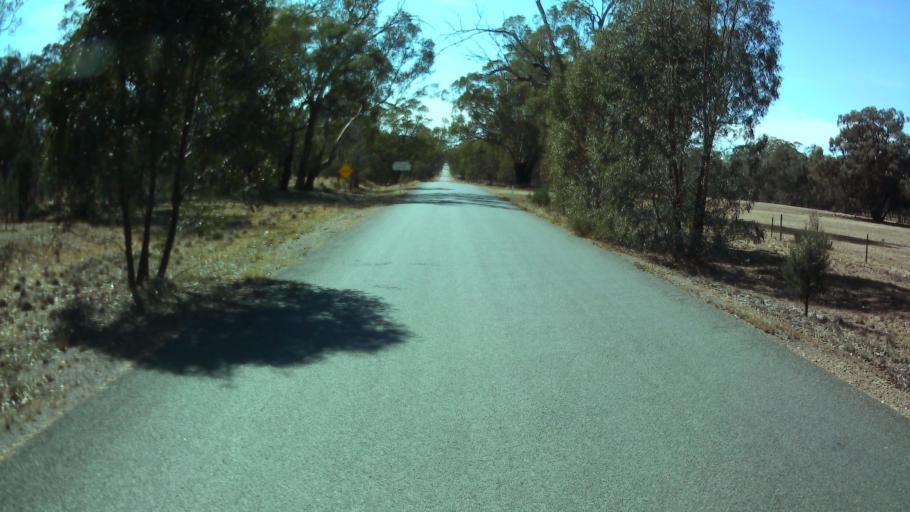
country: AU
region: New South Wales
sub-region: Weddin
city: Grenfell
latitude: -34.1151
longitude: 147.8456
